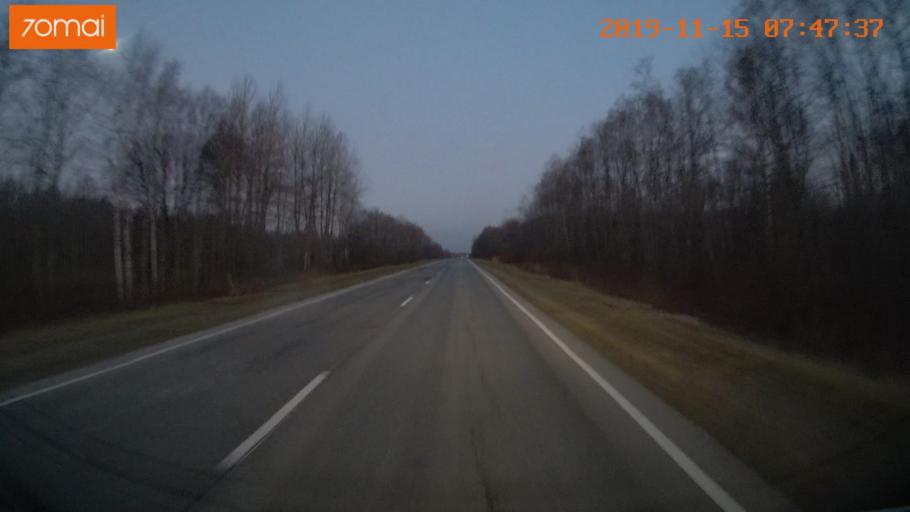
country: RU
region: Vologda
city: Sheksna
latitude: 58.8425
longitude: 38.2590
